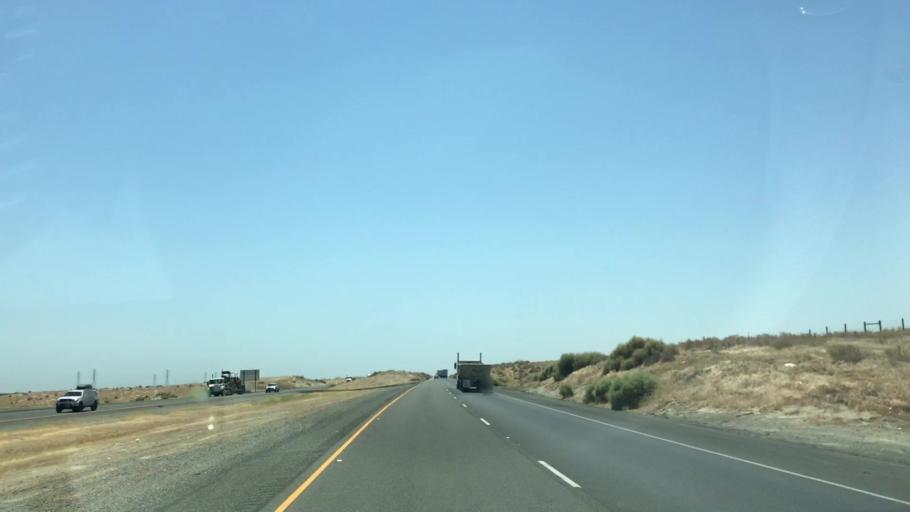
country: US
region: California
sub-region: Fresno County
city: Mendota
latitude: 36.5193
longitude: -120.4740
